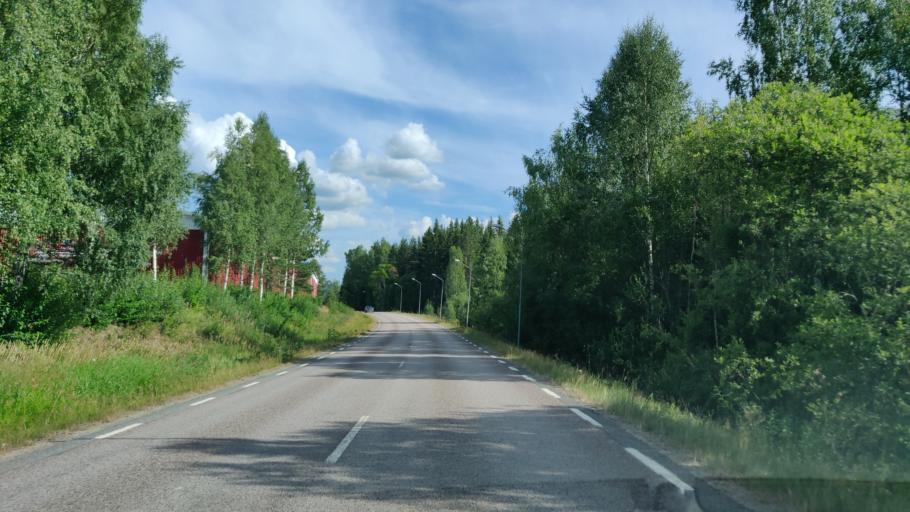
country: SE
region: Vaermland
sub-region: Hagfors Kommun
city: Hagfors
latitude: 60.0695
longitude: 13.6335
